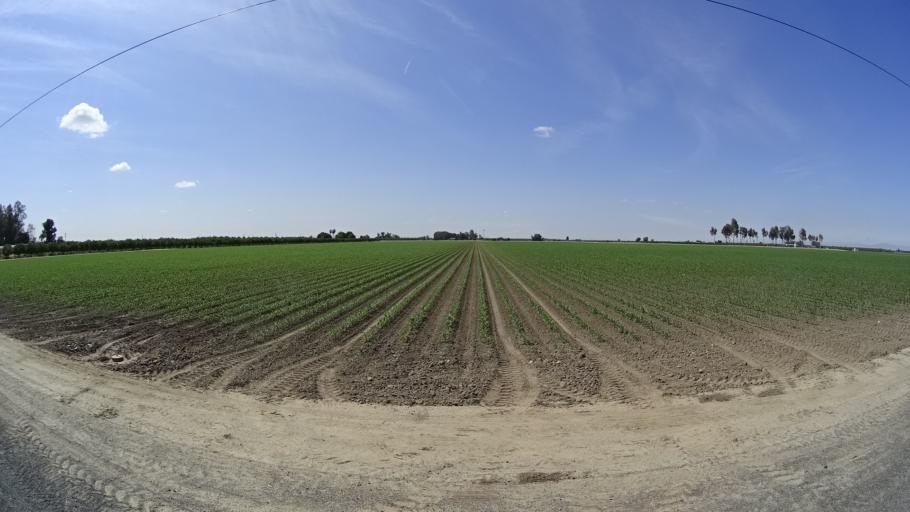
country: US
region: California
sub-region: Kings County
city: Armona
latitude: 36.2691
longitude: -119.7113
